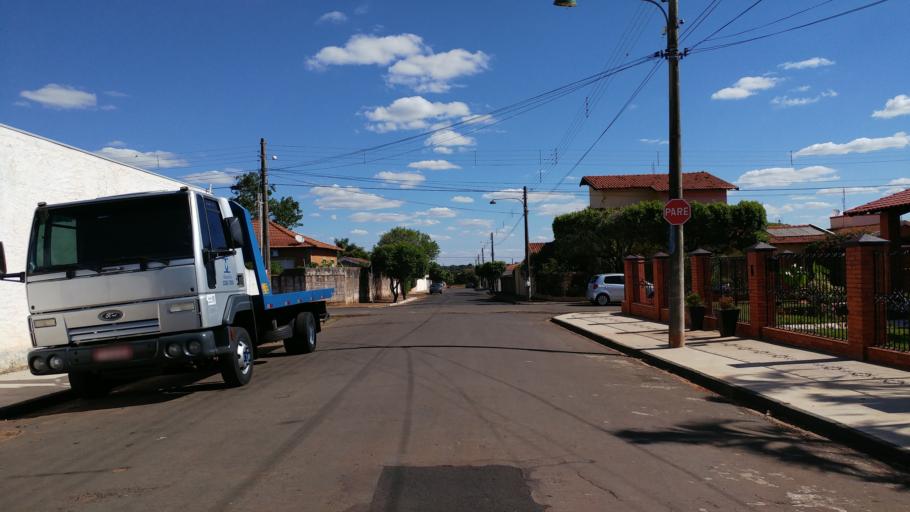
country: BR
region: Sao Paulo
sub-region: Paraguacu Paulista
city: Paraguacu Paulista
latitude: -22.4148
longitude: -50.5857
